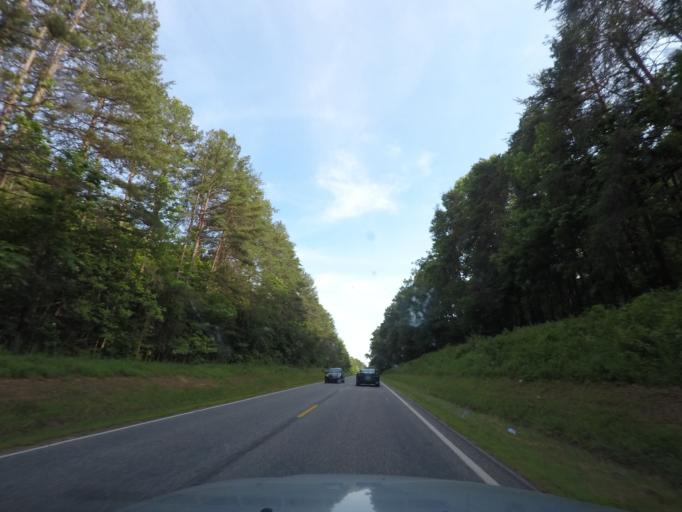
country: US
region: Virginia
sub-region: Mecklenburg County
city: Clarksville
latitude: 36.5620
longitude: -78.5425
